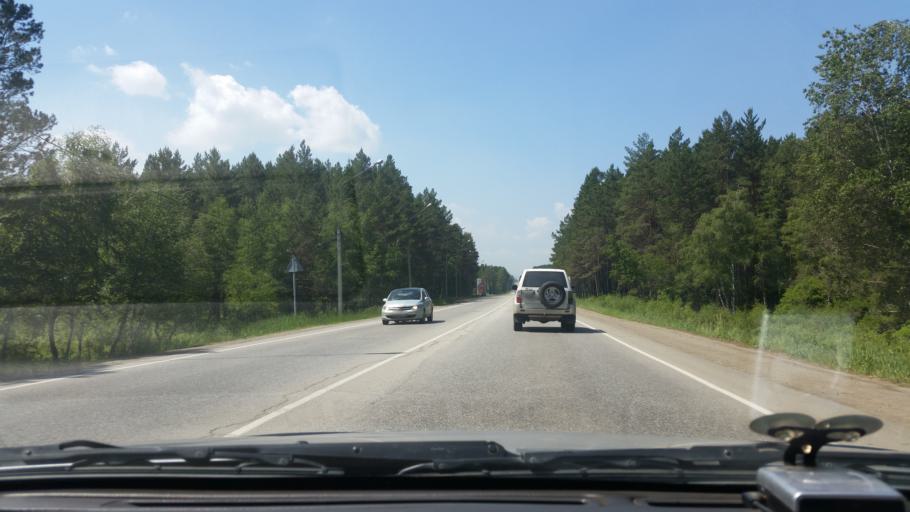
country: RU
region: Irkutsk
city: Shelekhov
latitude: 52.2175
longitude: 104.1288
